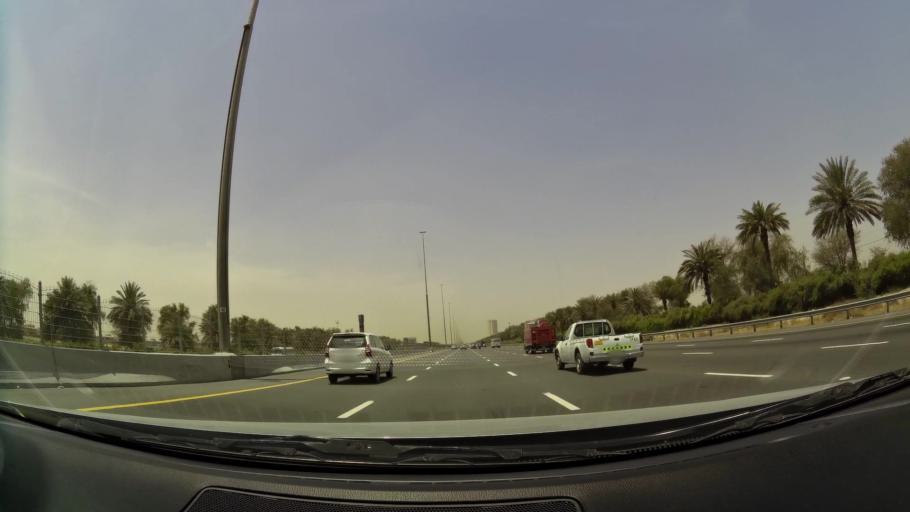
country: AE
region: Dubai
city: Dubai
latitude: 25.1064
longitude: 55.3403
